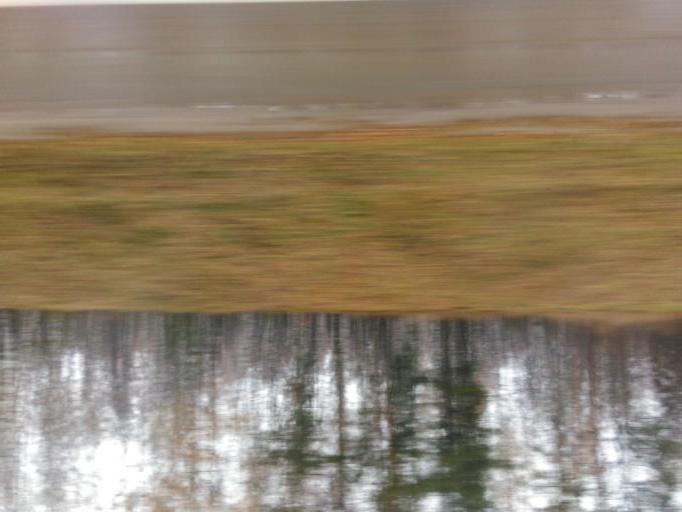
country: RU
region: Tatarstan
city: Osinovo
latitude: 55.8326
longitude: 48.8496
